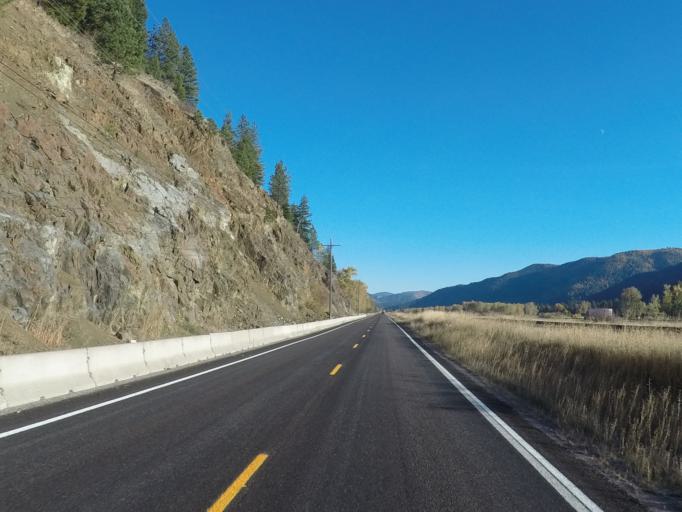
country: US
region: Montana
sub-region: Missoula County
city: Bonner-West Riverside
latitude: 46.8246
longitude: -113.8073
